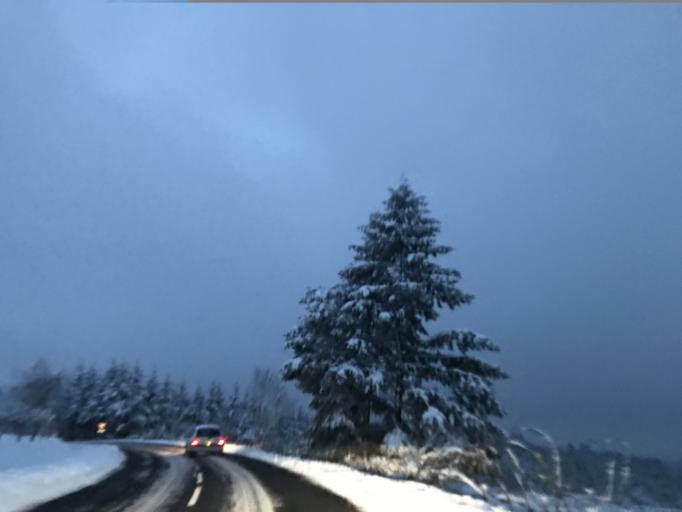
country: FR
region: Auvergne
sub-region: Departement du Puy-de-Dome
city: Courpiere
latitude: 45.7224
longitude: 3.5848
